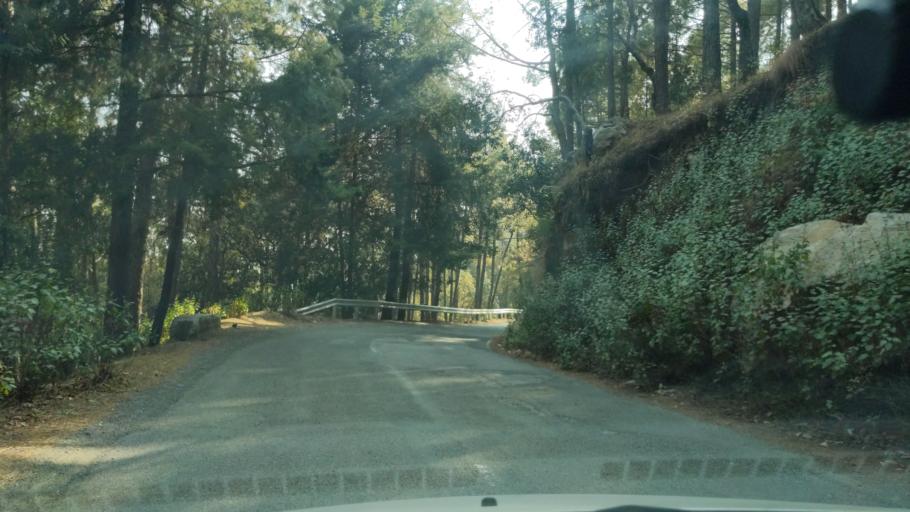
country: IN
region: Uttarakhand
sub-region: Naini Tal
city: Bhowali
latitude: 29.3987
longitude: 79.5380
